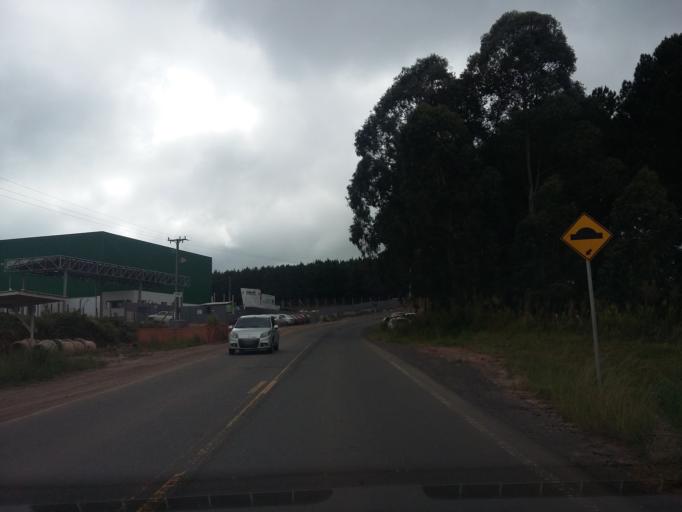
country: BR
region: Santa Catarina
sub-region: Lages
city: Lages
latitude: -27.8167
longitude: -50.2643
